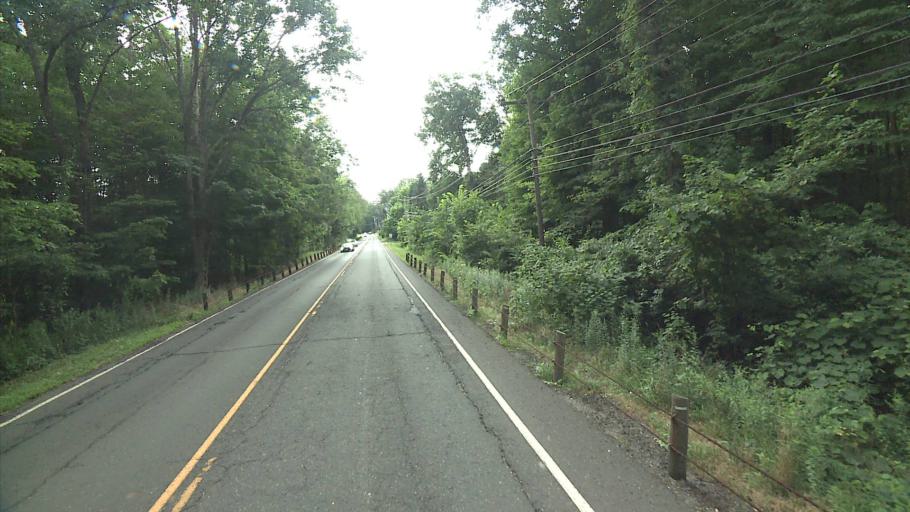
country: US
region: Connecticut
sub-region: New Haven County
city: Oxford
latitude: 41.4541
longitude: -73.1472
